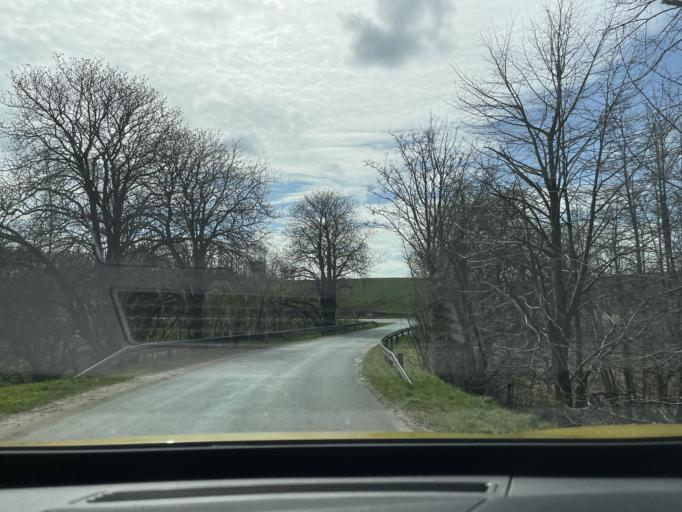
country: DK
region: Central Jutland
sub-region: Favrskov Kommune
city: Hinnerup
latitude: 56.3050
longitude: 10.0976
